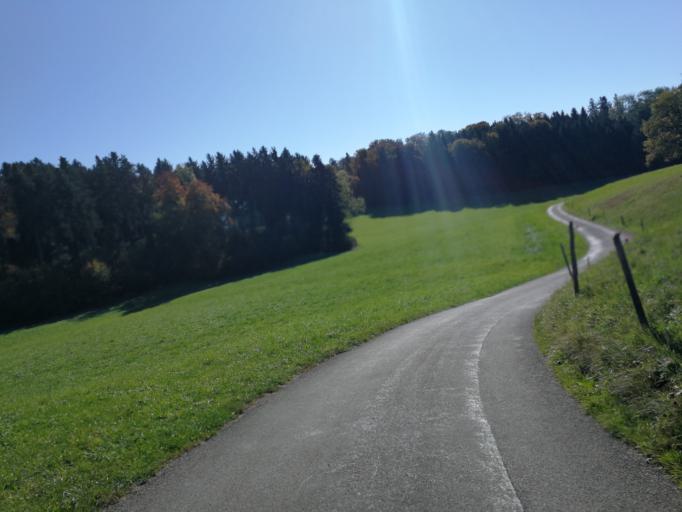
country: CH
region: Zurich
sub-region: Bezirk Meilen
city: Hombrechtikon
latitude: 47.2624
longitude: 8.7844
